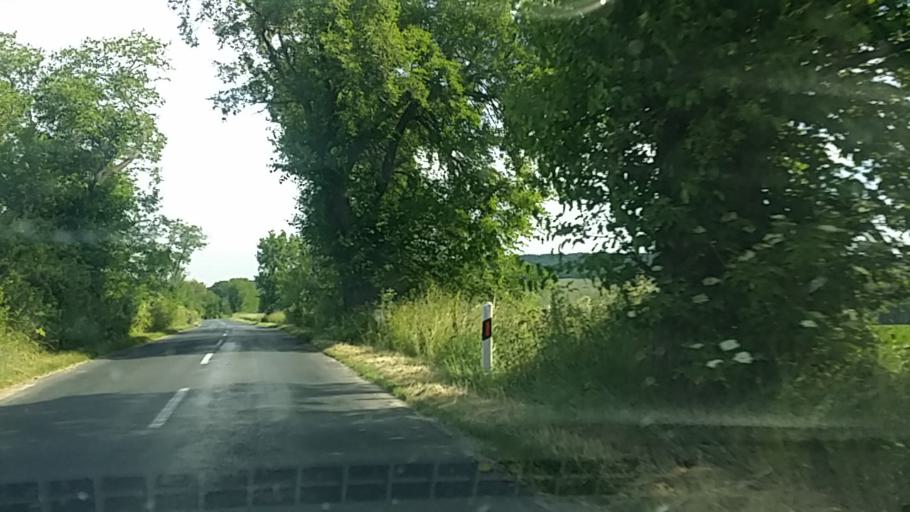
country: HU
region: Komarom-Esztergom
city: Bajna
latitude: 47.6808
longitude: 18.5722
